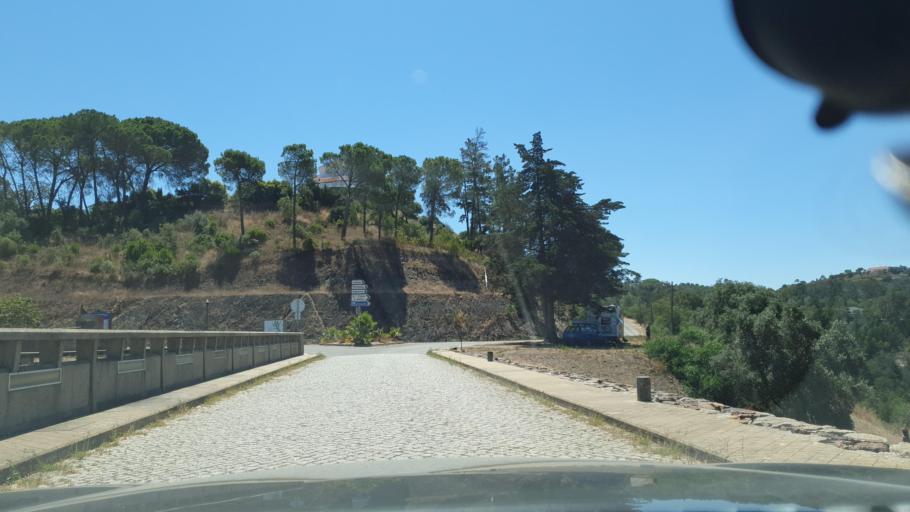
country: PT
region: Beja
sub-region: Odemira
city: Odemira
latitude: 37.5129
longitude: -8.4411
